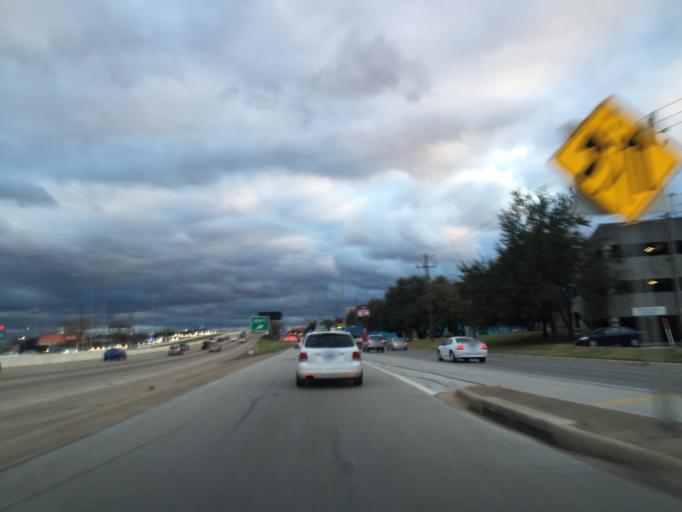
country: US
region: Texas
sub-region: Williamson County
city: Jollyville
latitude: 30.4048
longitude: -97.7458
